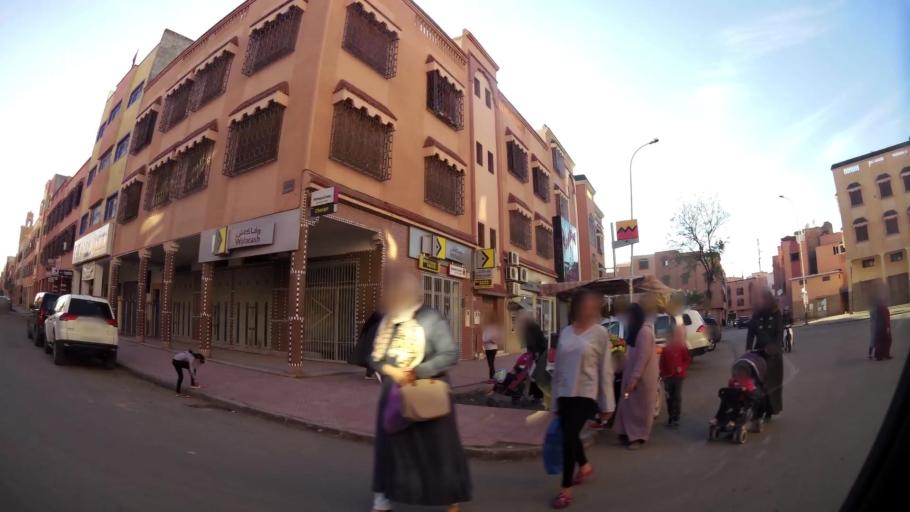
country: MA
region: Marrakech-Tensift-Al Haouz
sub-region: Marrakech
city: Marrakesh
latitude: 31.6188
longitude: -8.0604
